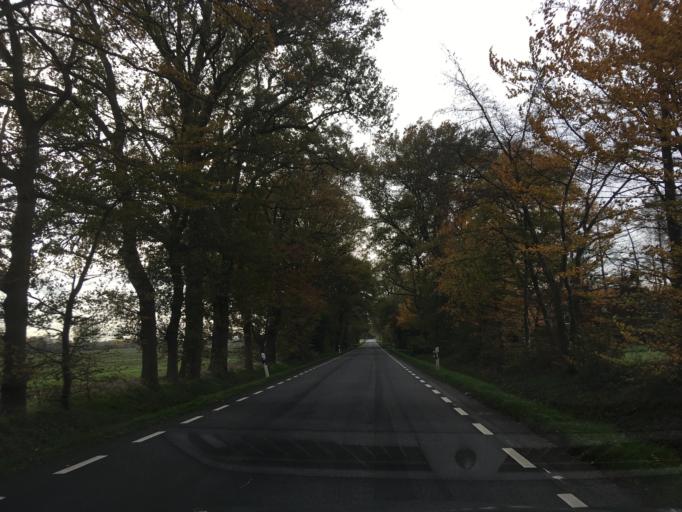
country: DE
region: North Rhine-Westphalia
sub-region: Regierungsbezirk Munster
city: Vreden
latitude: 52.0605
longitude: 6.8783
